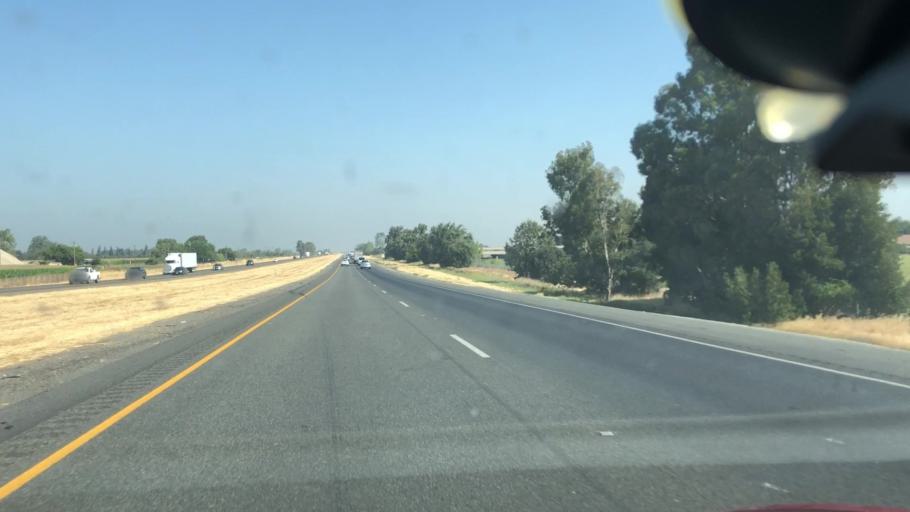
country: US
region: California
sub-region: Sacramento County
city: Walnut Grove
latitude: 38.3239
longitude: -121.4659
